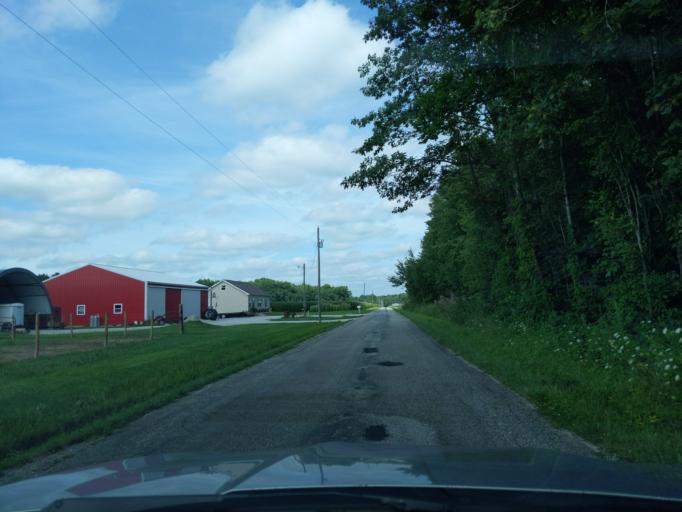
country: US
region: Indiana
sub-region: Ripley County
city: Osgood
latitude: 39.2379
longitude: -85.3562
